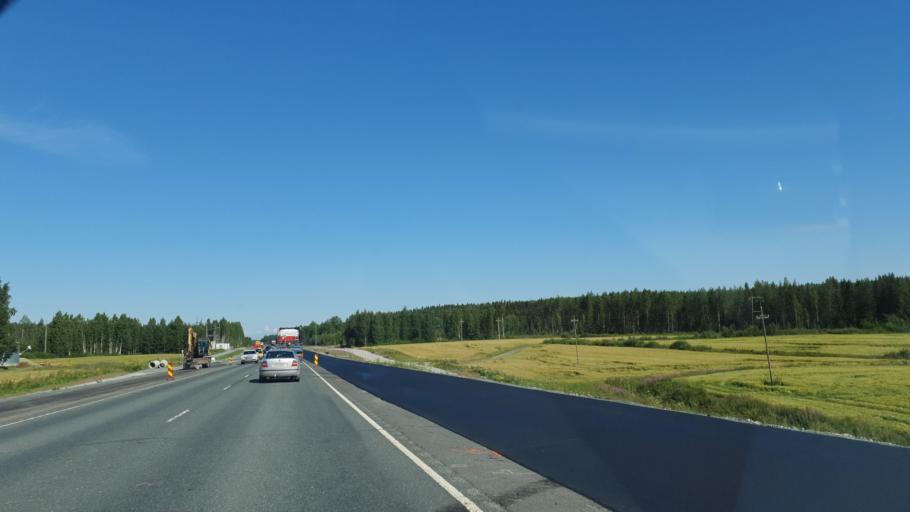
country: FI
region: Northern Savo
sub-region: Ylae-Savo
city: Lapinlahti
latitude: 63.2864
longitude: 27.4550
